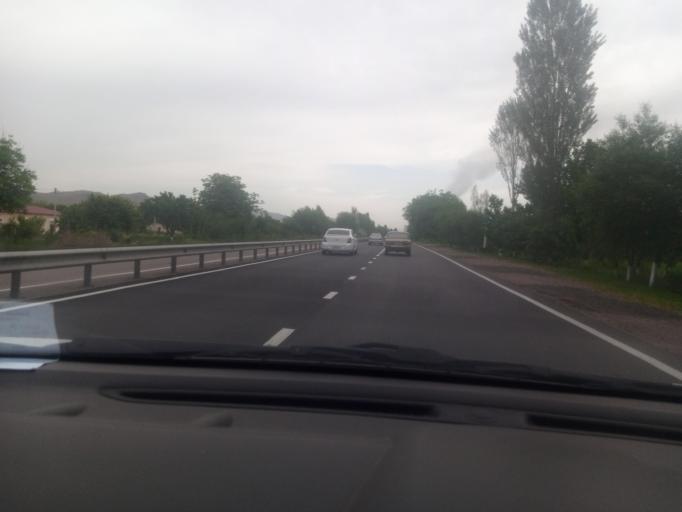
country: UZ
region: Toshkent
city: Ohangaron
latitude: 40.9074
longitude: 69.7406
